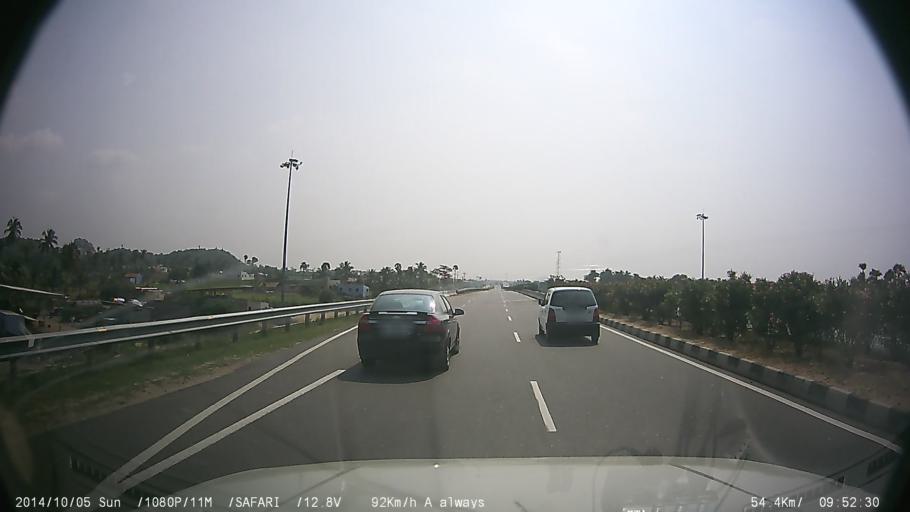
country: IN
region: Tamil Nadu
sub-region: Salem
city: Konganapuram
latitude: 11.4932
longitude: 77.8854
